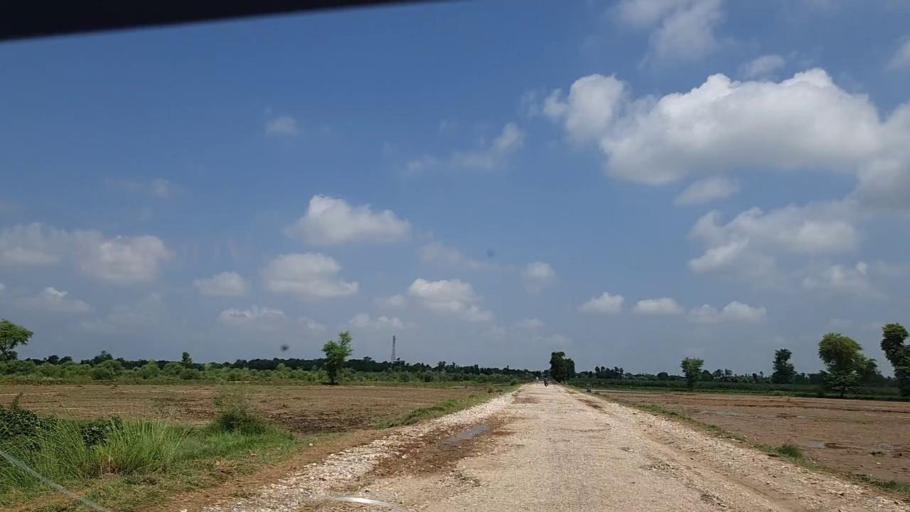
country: PK
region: Sindh
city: Tharu Shah
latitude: 26.9036
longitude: 68.0384
